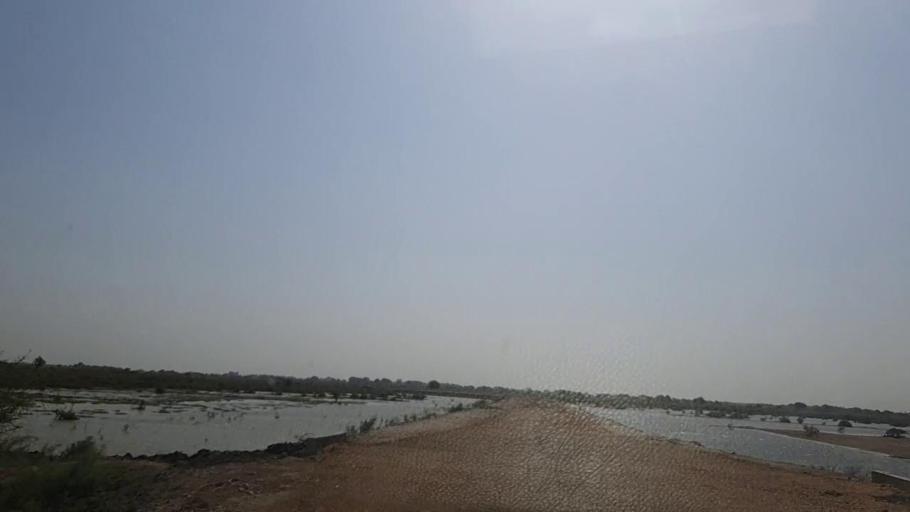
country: PK
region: Sindh
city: Daro Mehar
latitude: 24.7053
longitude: 68.1270
